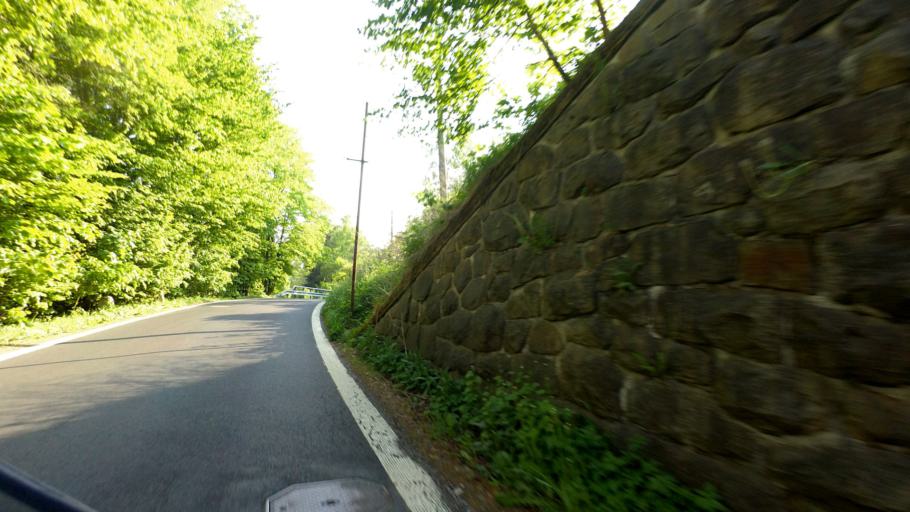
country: CZ
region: Ustecky
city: Dolni Poustevna
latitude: 50.9919
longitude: 14.2925
